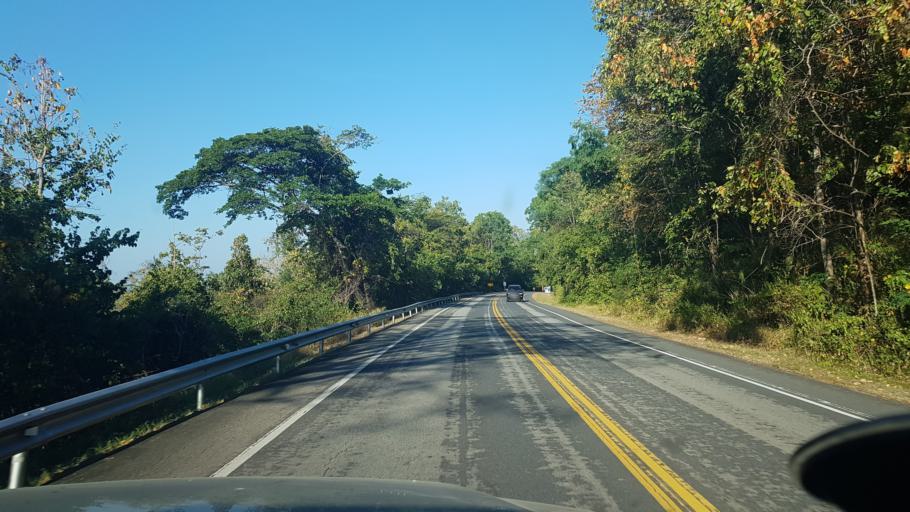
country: TH
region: Phetchabun
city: Lom Sak
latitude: 16.7396
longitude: 101.4136
